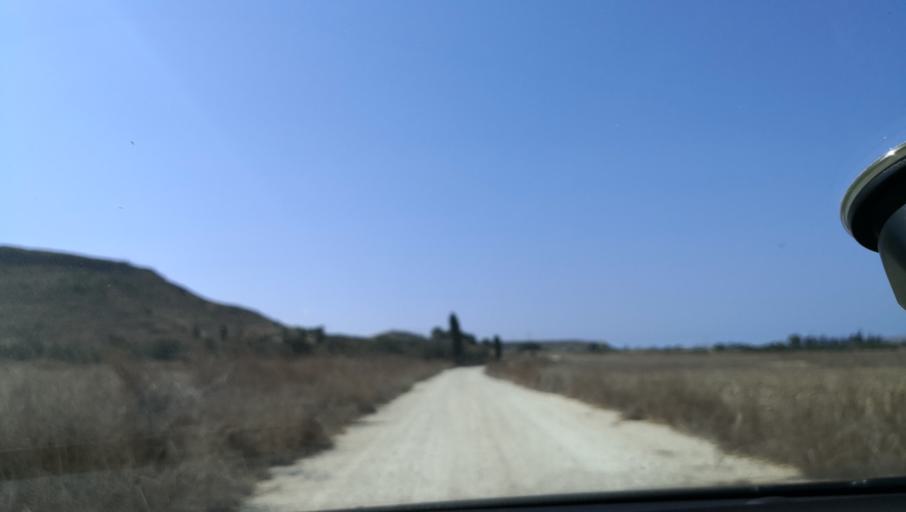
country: CY
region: Lefkosia
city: Mammari
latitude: 35.1766
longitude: 33.2167
